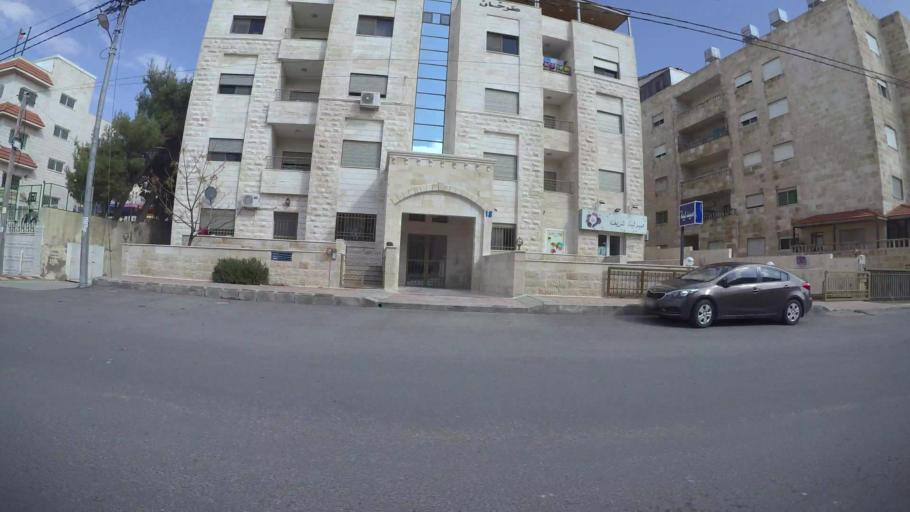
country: JO
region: Amman
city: Al Jubayhah
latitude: 32.0203
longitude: 35.8541
